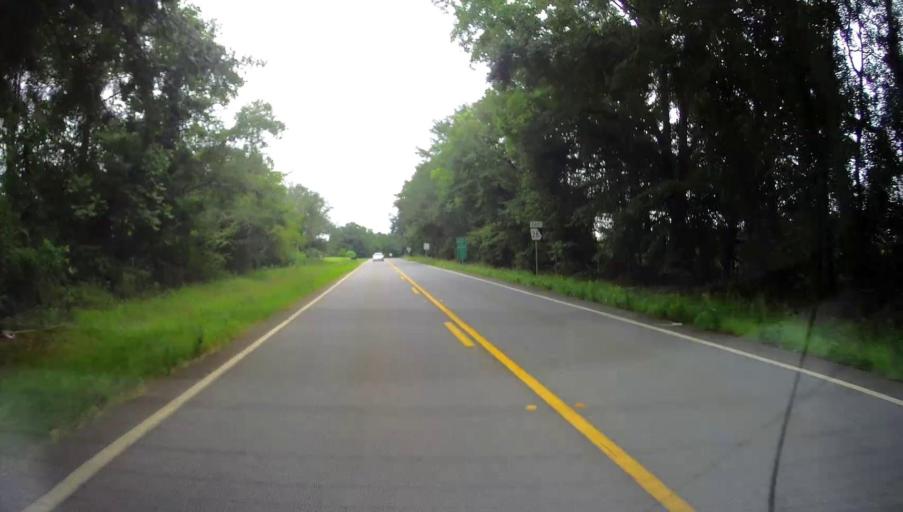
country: US
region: Georgia
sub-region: Schley County
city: Ellaville
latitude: 32.2569
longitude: -84.4098
